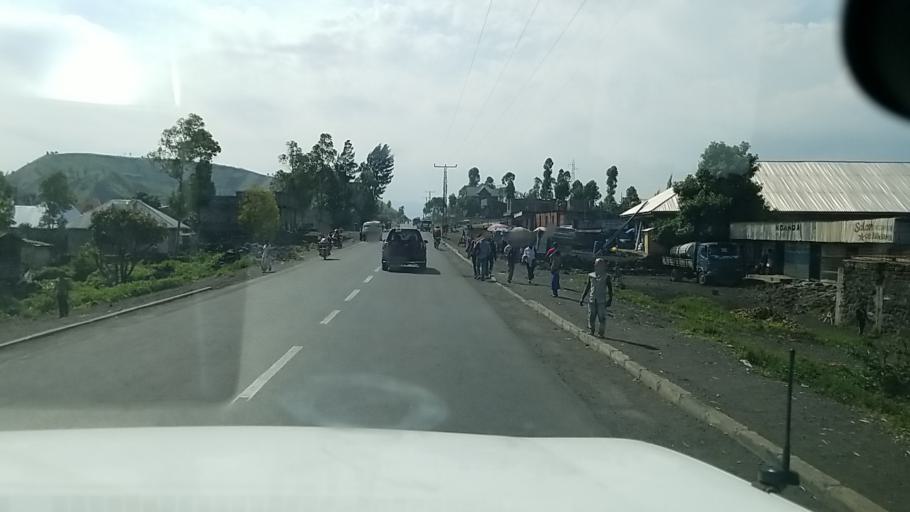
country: CD
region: Nord Kivu
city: Goma
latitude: -1.6345
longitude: 29.1721
